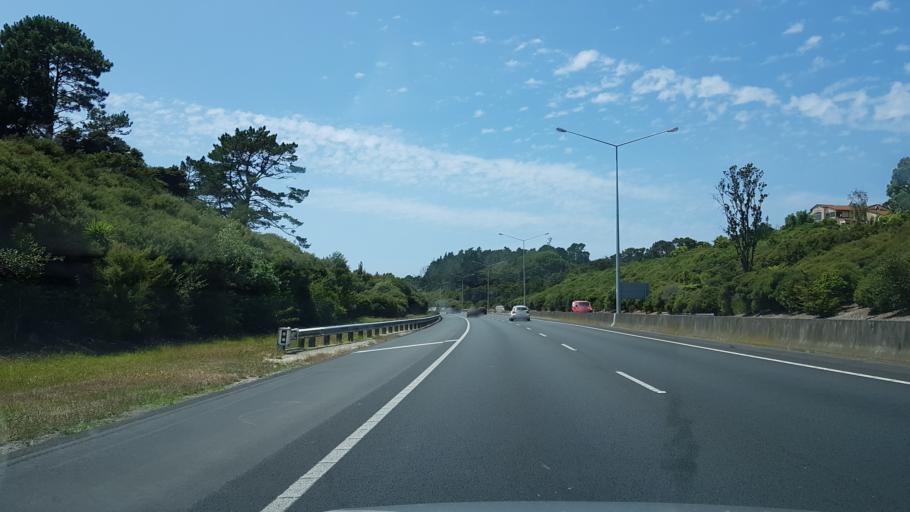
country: NZ
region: Auckland
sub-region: Auckland
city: Rothesay Bay
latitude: -36.7643
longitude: 174.6958
